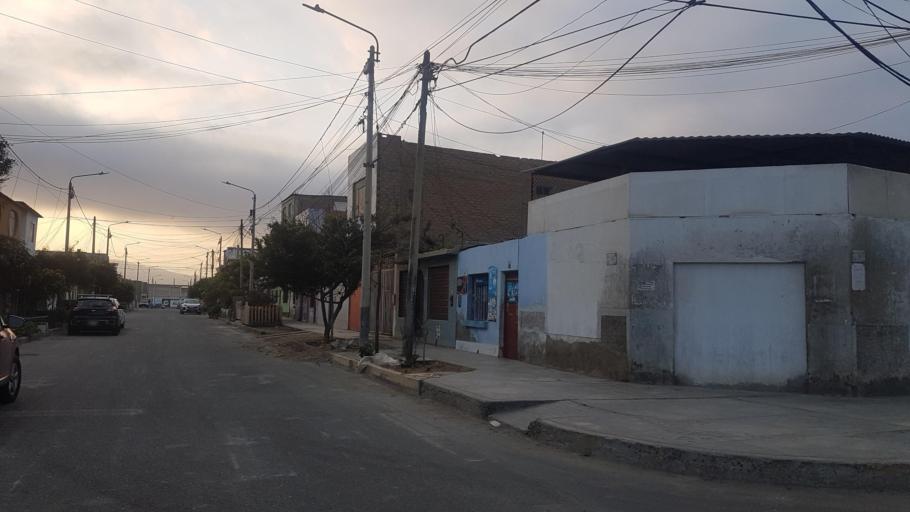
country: PE
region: Ancash
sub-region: Provincia de Santa
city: Chimbote
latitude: -9.0948
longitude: -78.5728
